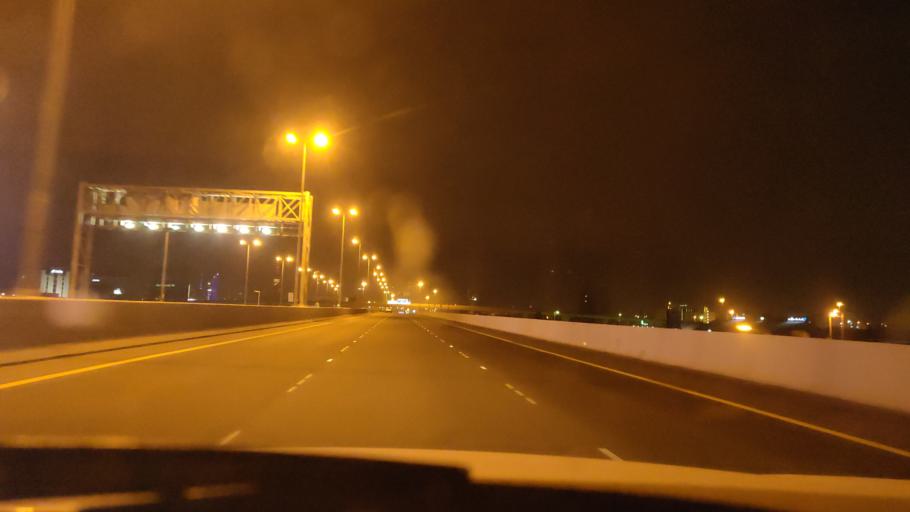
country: KW
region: Al Asimah
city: Ash Shamiyah
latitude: 29.3378
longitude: 47.9405
